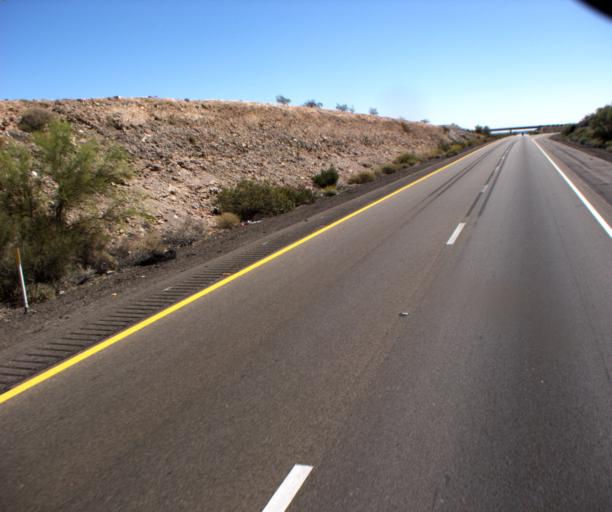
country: US
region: Arizona
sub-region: La Paz County
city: Salome
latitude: 33.6100
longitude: -113.6280
